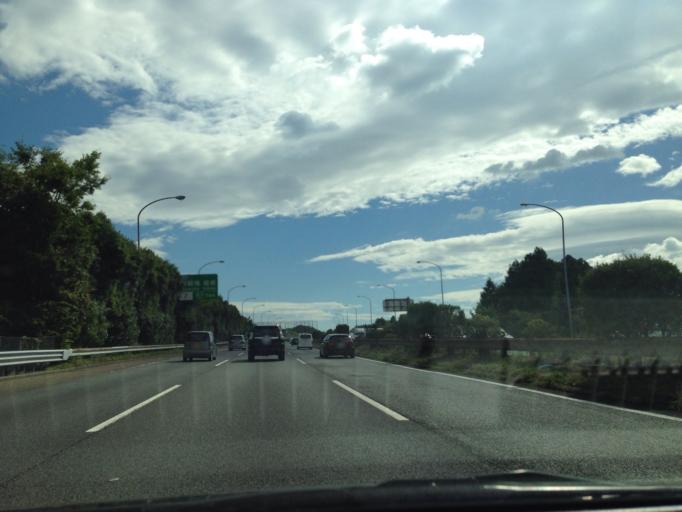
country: JP
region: Shizuoka
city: Gotemba
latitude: 35.3047
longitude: 138.9600
